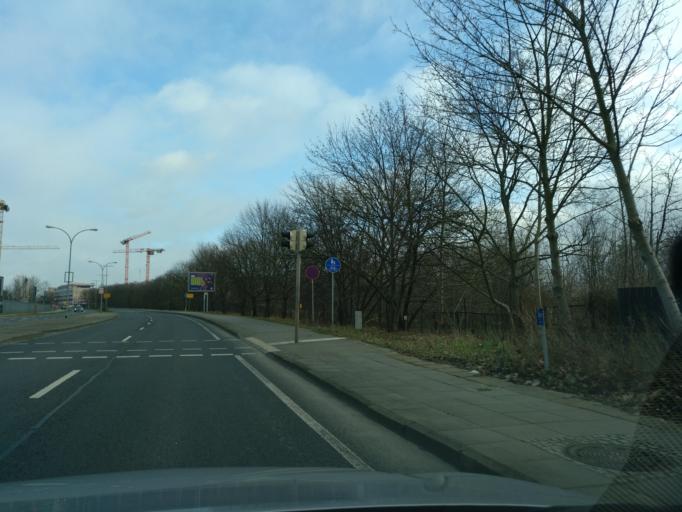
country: DE
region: Berlin
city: Altglienicke
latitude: 52.3947
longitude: 13.5343
